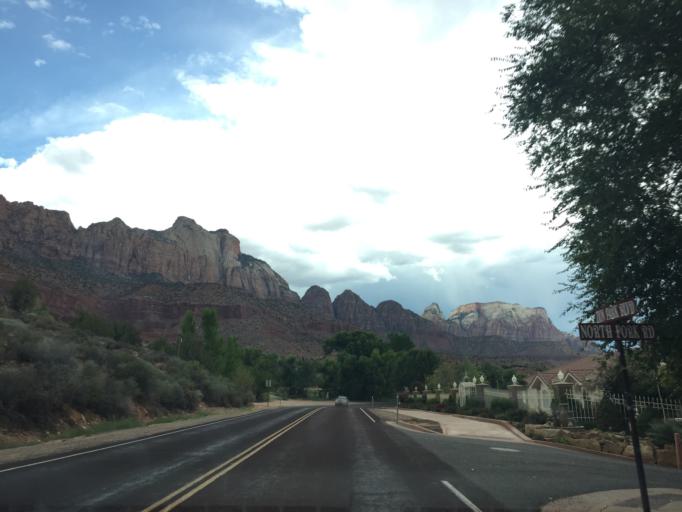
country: US
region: Utah
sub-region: Washington County
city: Hildale
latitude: 37.1721
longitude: -113.0134
